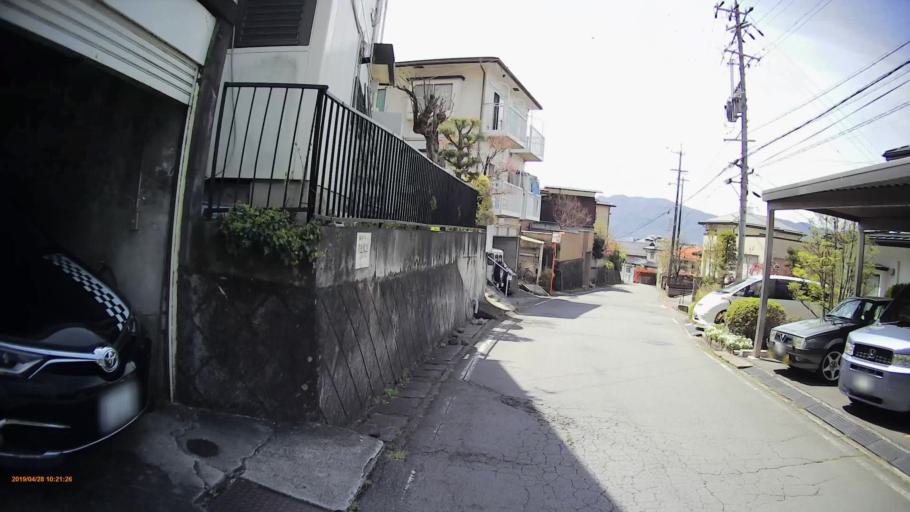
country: JP
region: Nagano
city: Suwa
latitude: 36.0626
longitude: 138.1118
